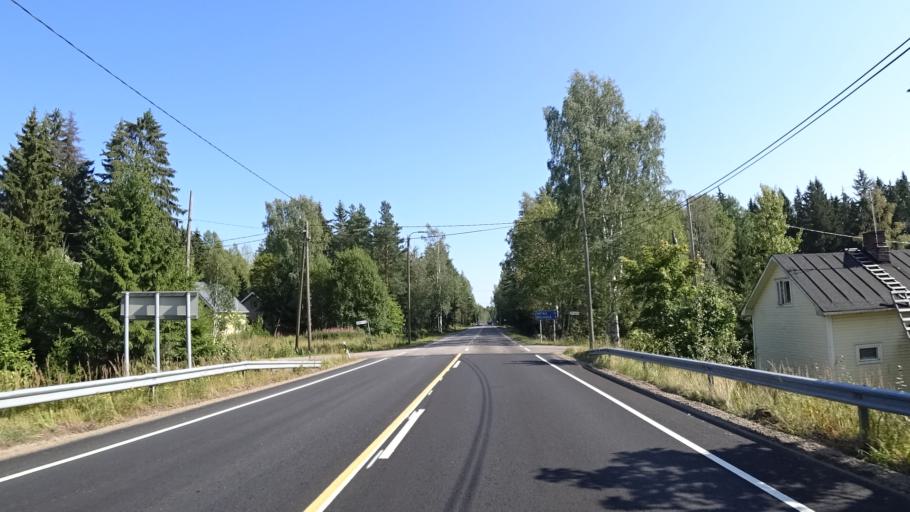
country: FI
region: Kymenlaakso
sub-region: Kotka-Hamina
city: Karhula
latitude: 60.5464
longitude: 26.9165
